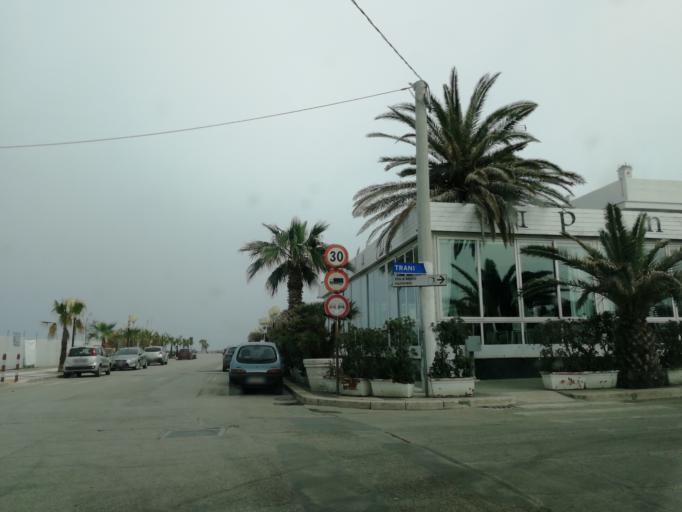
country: IT
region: Apulia
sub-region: Provincia di Barletta - Andria - Trani
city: Barletta
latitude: 41.3197
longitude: 16.2993
